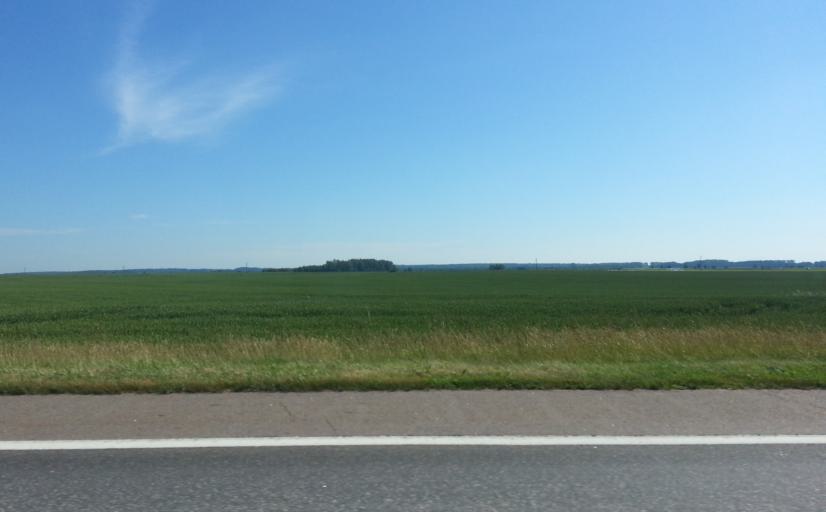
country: LT
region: Vilnius County
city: Ukmerge
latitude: 55.3195
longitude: 24.7768
